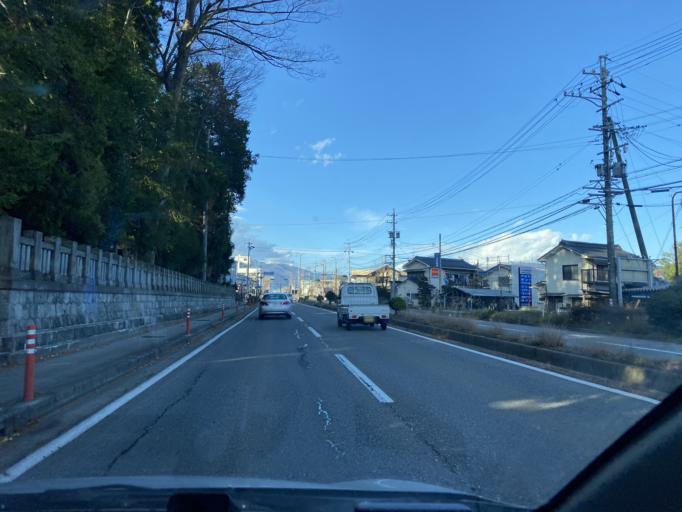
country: JP
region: Nagano
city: Omachi
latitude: 36.5074
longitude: 137.8541
